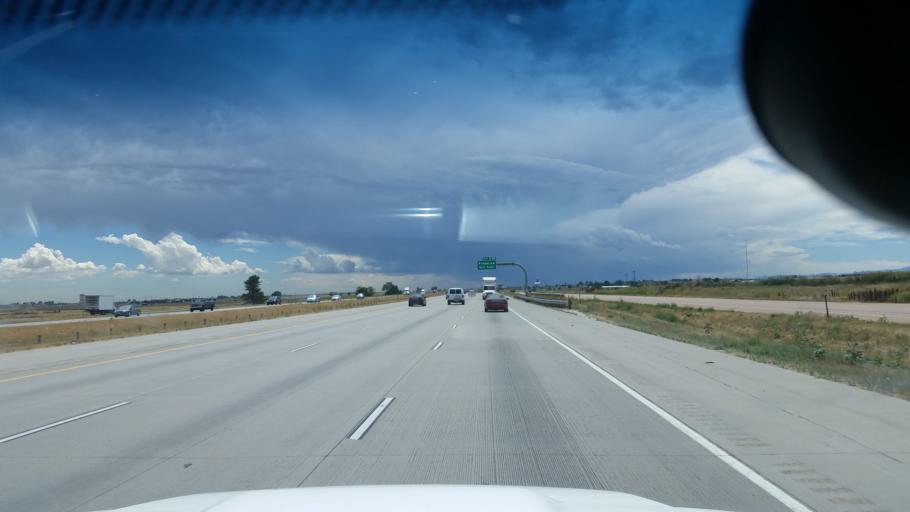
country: US
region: Colorado
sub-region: Weld County
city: Frederick
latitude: 40.1020
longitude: -104.9807
